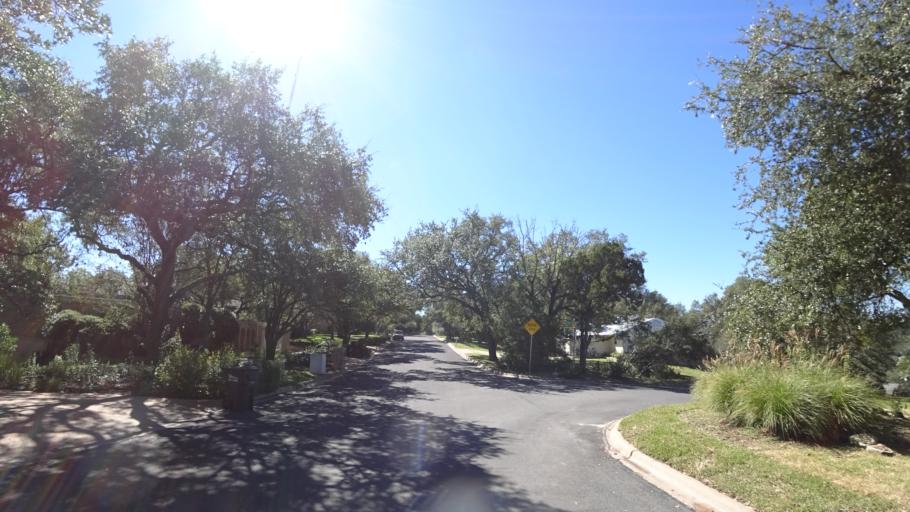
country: US
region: Texas
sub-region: Travis County
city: West Lake Hills
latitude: 30.3130
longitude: -97.7930
